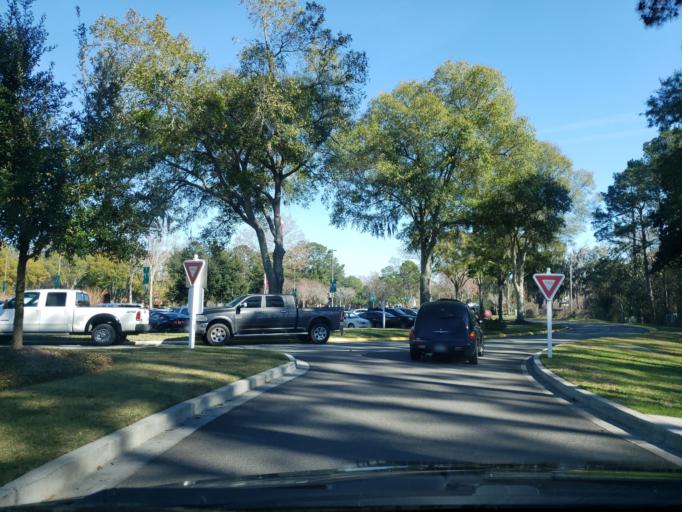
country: US
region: Georgia
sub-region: Chatham County
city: Montgomery
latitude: 31.9846
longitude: -81.1546
